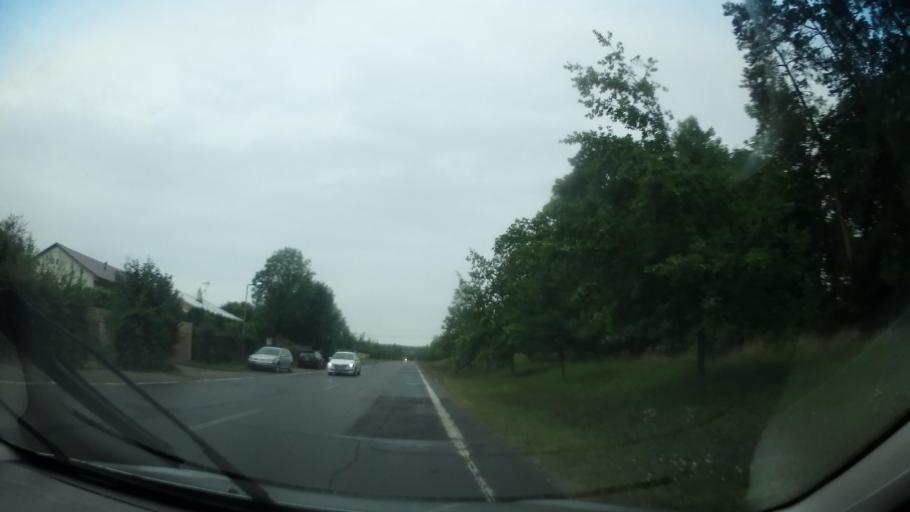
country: CZ
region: Central Bohemia
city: Milovice
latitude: 50.2309
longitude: 14.8924
